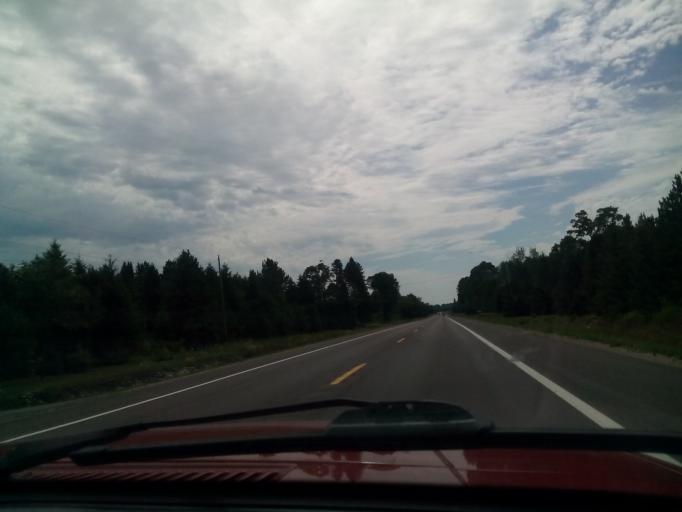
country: US
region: Michigan
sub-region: Schoolcraft County
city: Manistique
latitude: 46.0754
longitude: -85.9583
